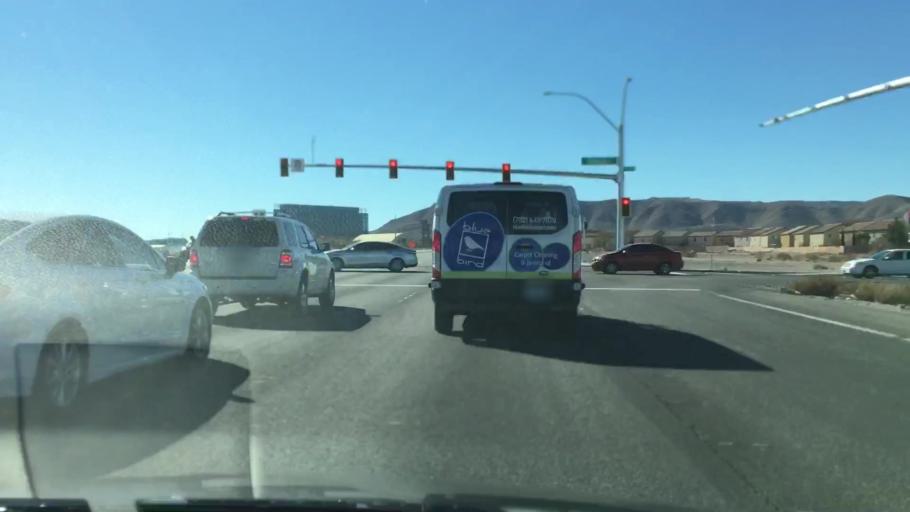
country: US
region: Nevada
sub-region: Clark County
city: Enterprise
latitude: 35.9731
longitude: -115.1624
